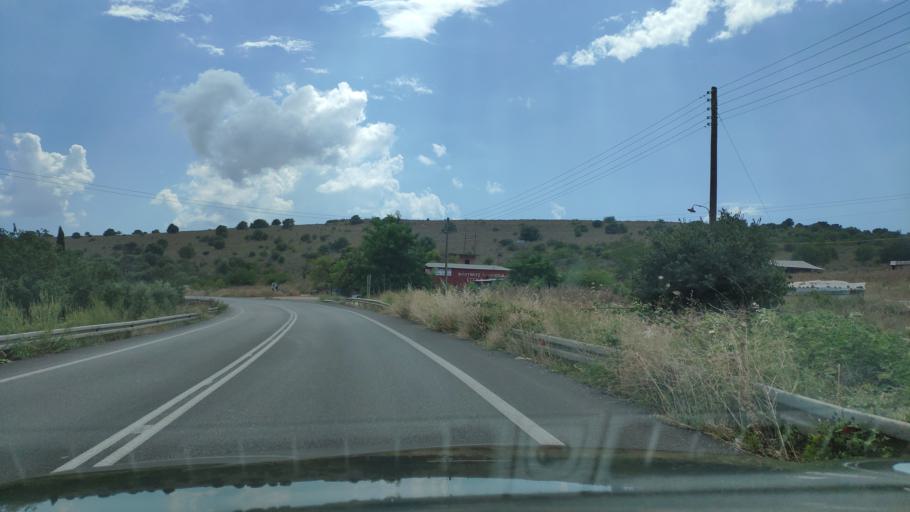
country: GR
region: West Greece
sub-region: Nomos Aitolias kai Akarnanias
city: Krikellos
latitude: 38.9140
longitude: 21.1700
